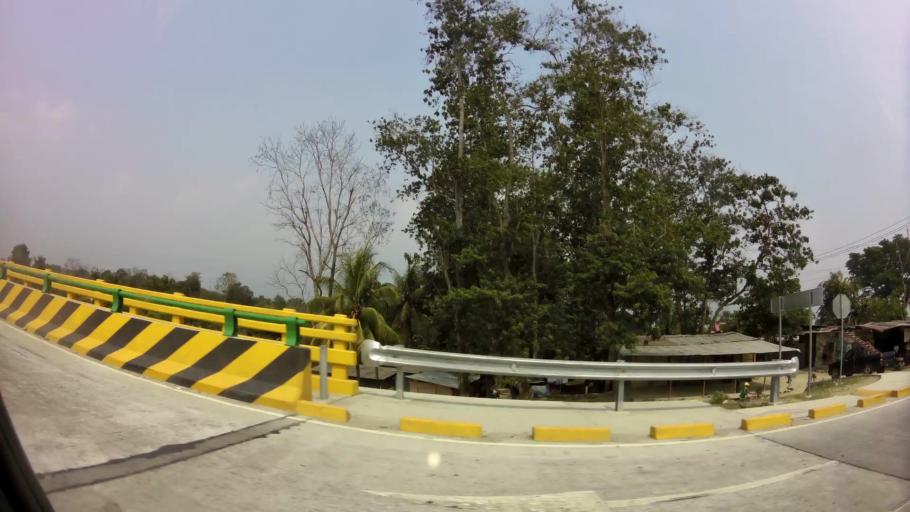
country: HN
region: Cortes
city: San Pedro Sula
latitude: 15.5162
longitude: -88.0024
